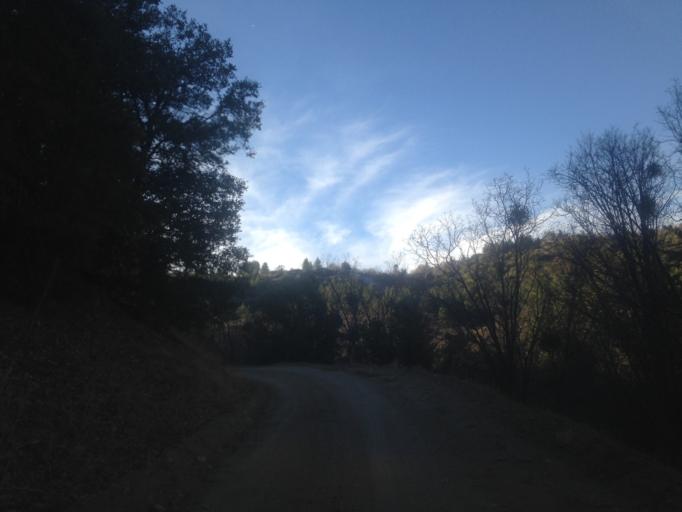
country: US
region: California
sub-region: San Bernardino County
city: Yucaipa
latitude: 34.1299
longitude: -117.0036
